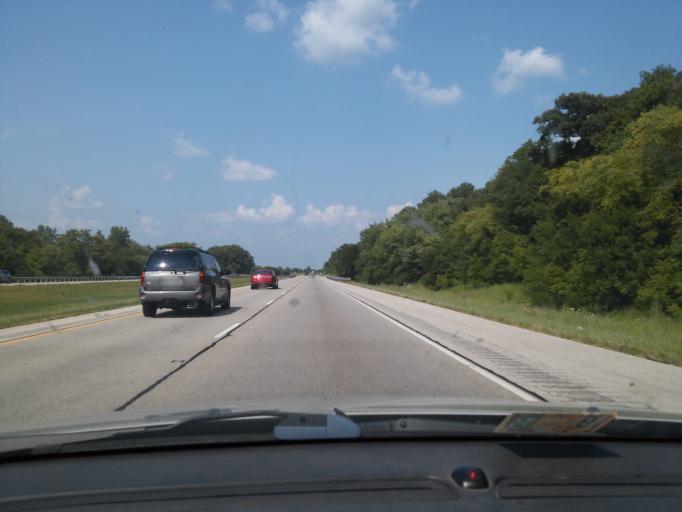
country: US
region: Illinois
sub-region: McLean County
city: Twin Grove
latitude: 40.3717
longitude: -89.0986
